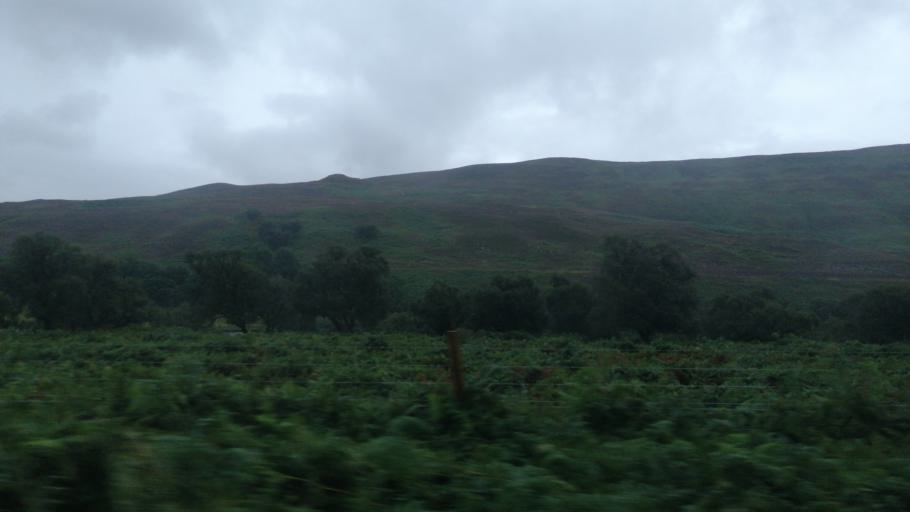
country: GB
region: Scotland
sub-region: Highland
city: Brora
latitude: 58.1412
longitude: -3.7111
